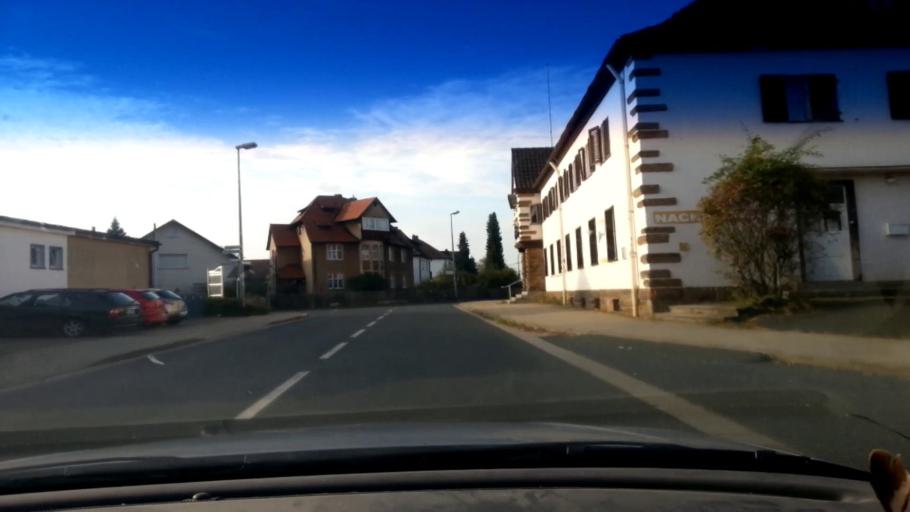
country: DE
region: Bavaria
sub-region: Upper Franconia
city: Hirschaid
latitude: 49.8192
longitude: 10.9910
